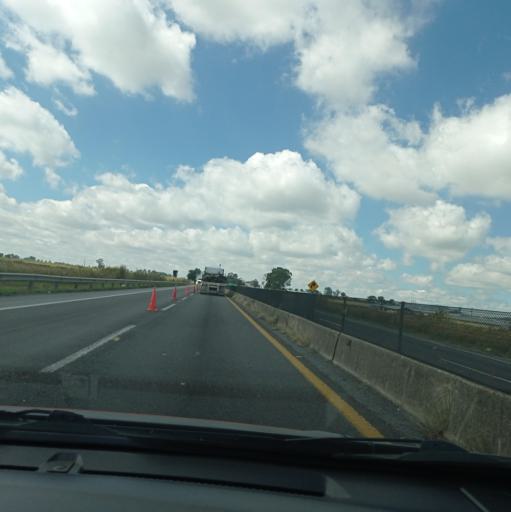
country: MX
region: Jalisco
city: Tepatitlan de Morelos
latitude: 20.9053
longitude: -102.6906
